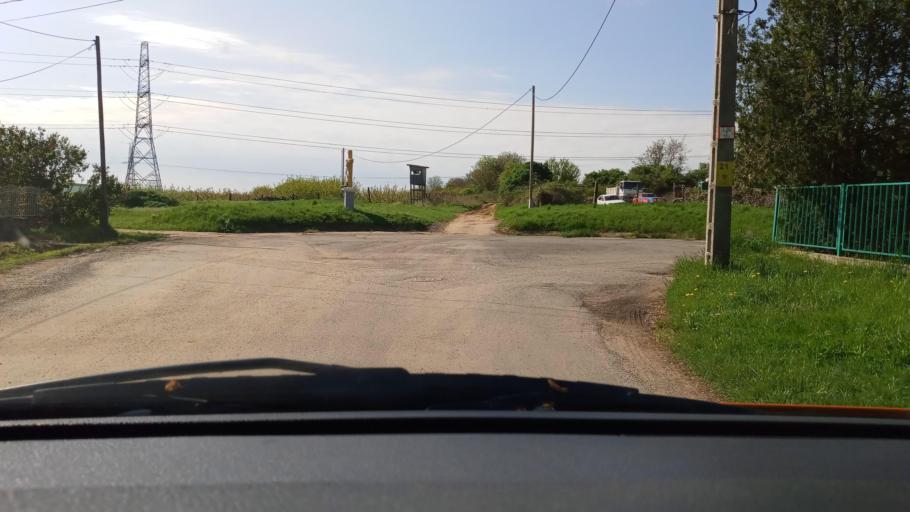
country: HU
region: Baranya
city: Hosszuheteny
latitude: 46.1051
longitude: 18.3444
